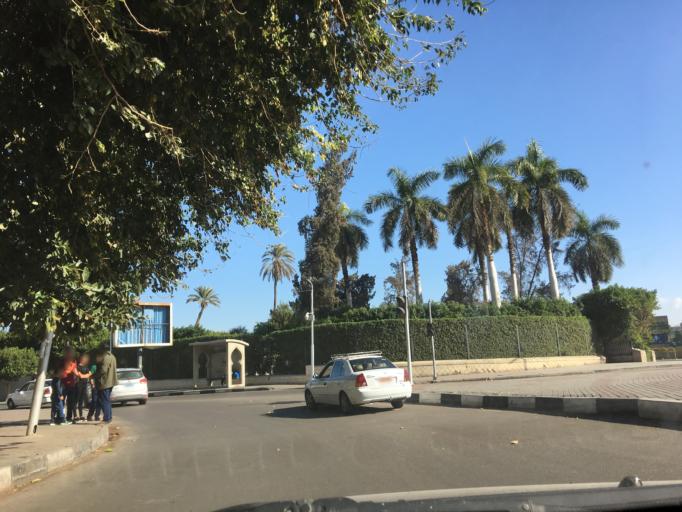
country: EG
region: Muhafazat al Qahirah
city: Cairo
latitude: 30.0437
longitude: 31.2269
